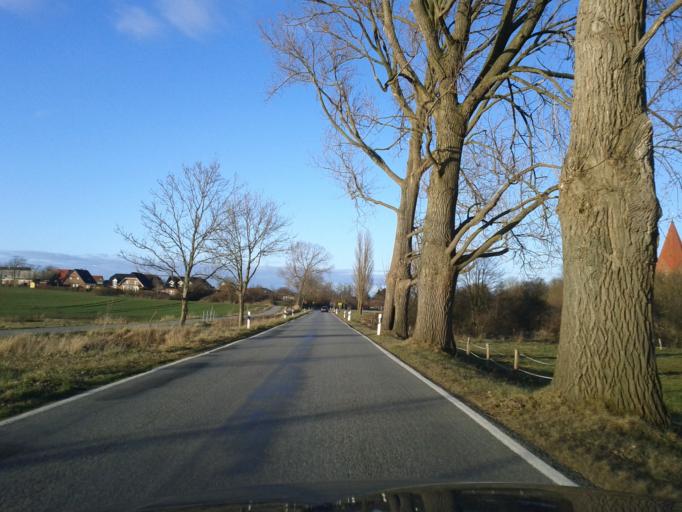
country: DE
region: Mecklenburg-Vorpommern
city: Blowatz
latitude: 53.9927
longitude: 11.4341
